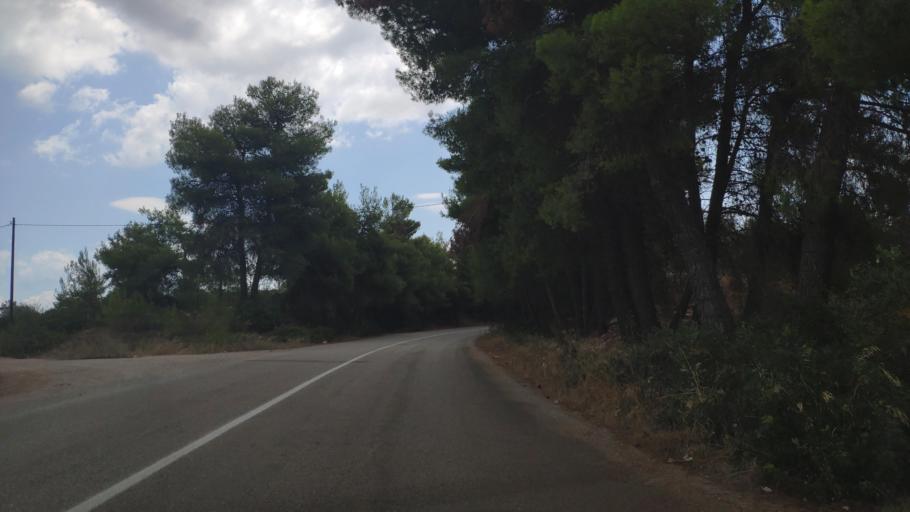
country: GR
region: Central Greece
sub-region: Nomos Fthiotidos
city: Malesina
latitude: 38.6286
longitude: 23.1790
